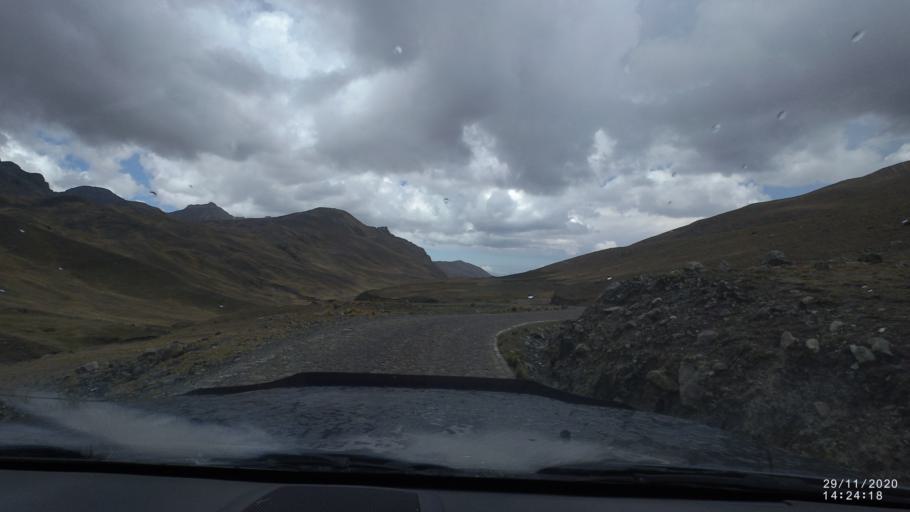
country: BO
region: Cochabamba
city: Sipe Sipe
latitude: -17.2543
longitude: -66.3797
